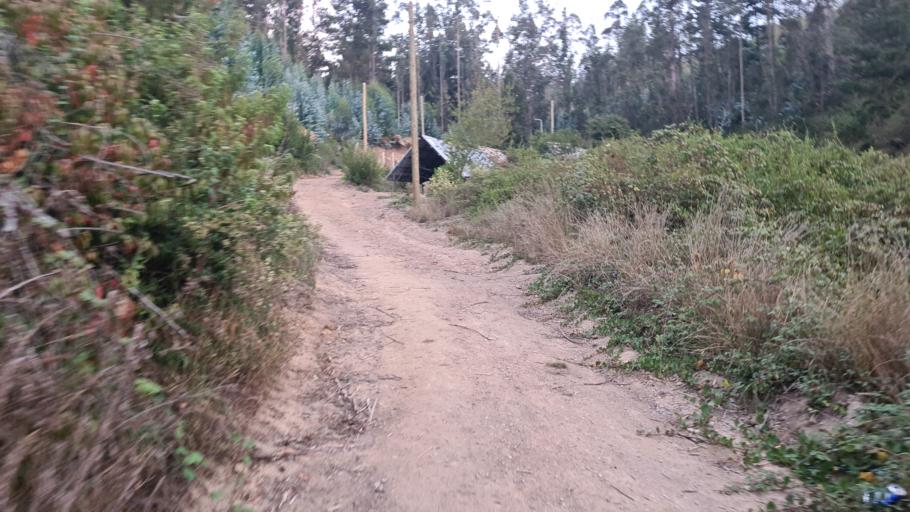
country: CL
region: Biobio
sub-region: Provincia de Concepcion
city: Penco
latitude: -36.7174
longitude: -72.9657
